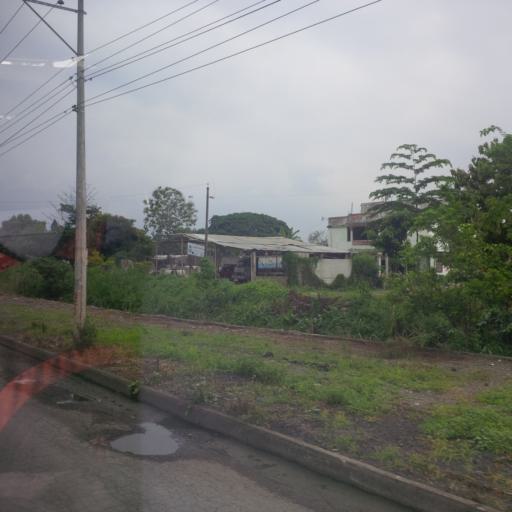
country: EC
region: Canar
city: La Troncal
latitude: -2.3348
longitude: -79.4003
